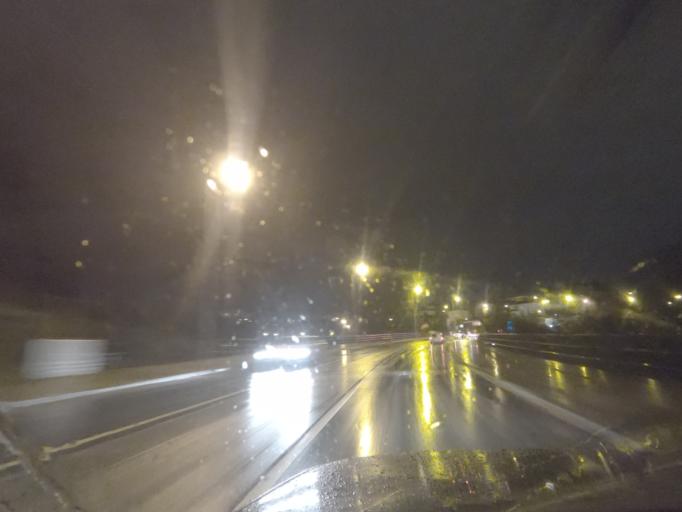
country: PT
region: Vila Real
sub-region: Vila Real
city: Vila Real
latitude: 41.3065
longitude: -7.7349
